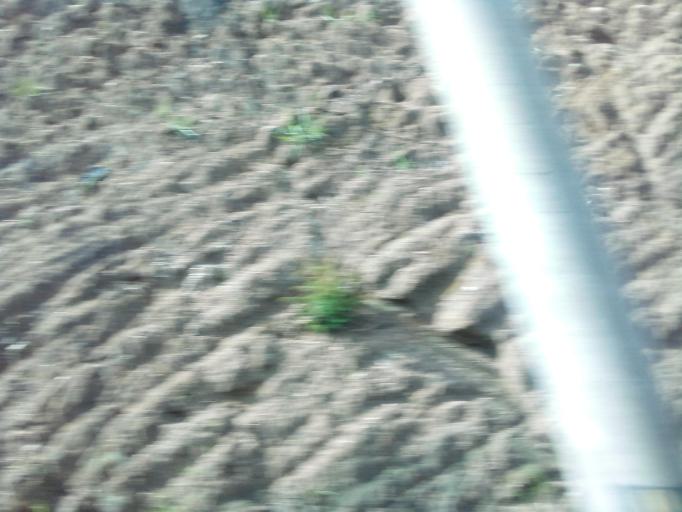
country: BR
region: Minas Gerais
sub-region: Raposos
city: Raposos
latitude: -19.8697
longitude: -43.8306
